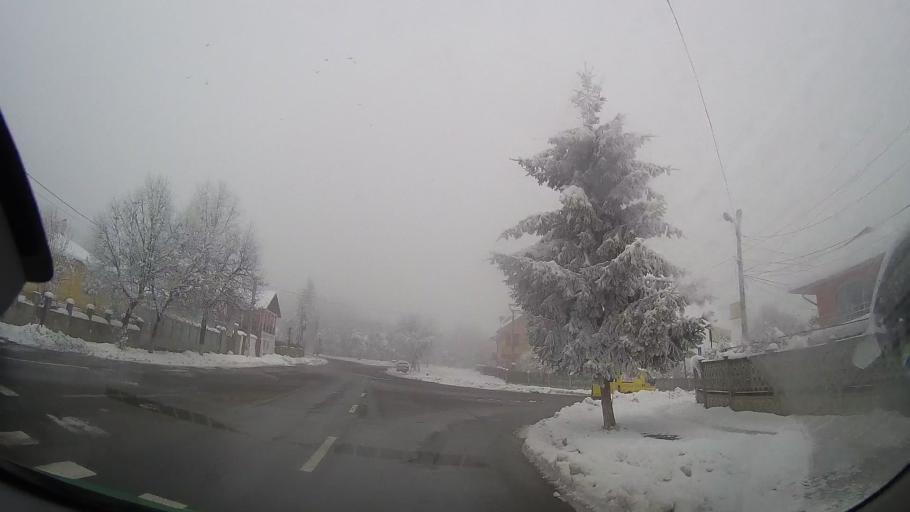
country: RO
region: Iasi
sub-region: Municipiul Pascani
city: Pascani
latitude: 47.2428
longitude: 26.7301
